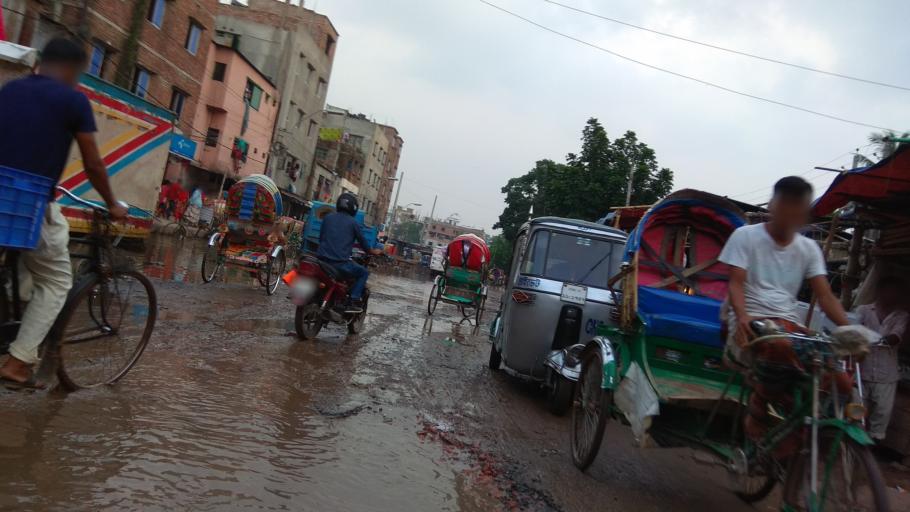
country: BD
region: Dhaka
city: Tungi
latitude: 23.8184
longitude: 90.3780
